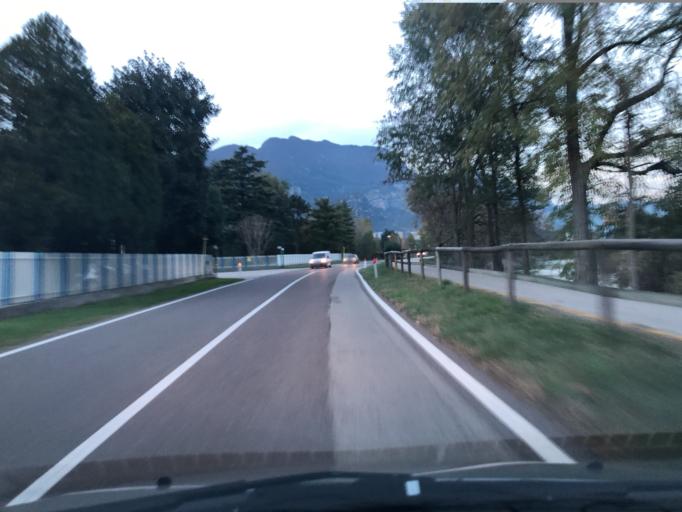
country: IT
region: Trentino-Alto Adige
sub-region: Provincia di Trento
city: Arco
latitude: 45.8986
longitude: 10.8802
